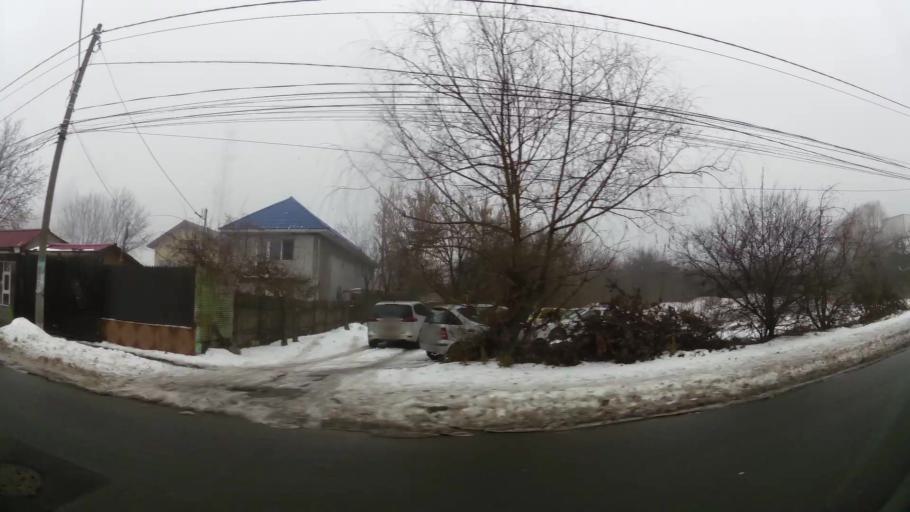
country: RO
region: Ilfov
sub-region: Comuna Chiajna
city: Rosu
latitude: 44.4748
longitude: 26.0121
